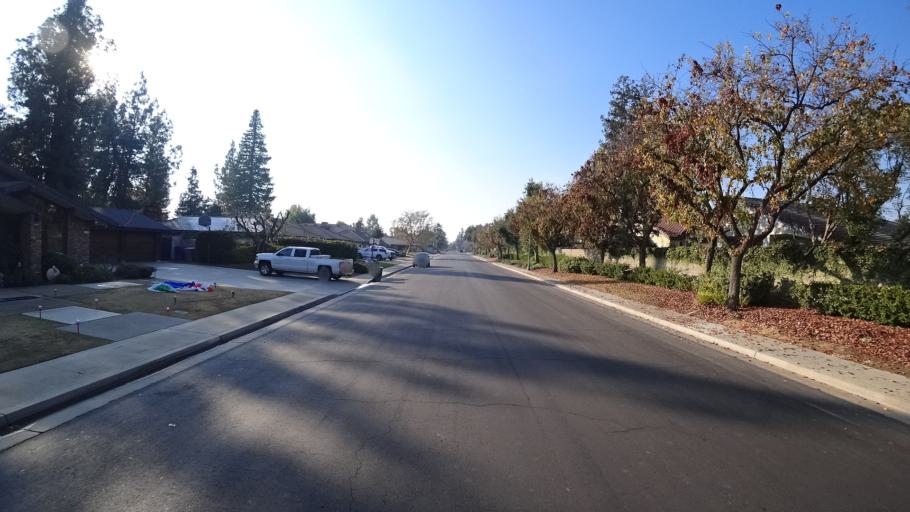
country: US
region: California
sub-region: Kern County
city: Greenacres
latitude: 35.3381
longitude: -119.0988
